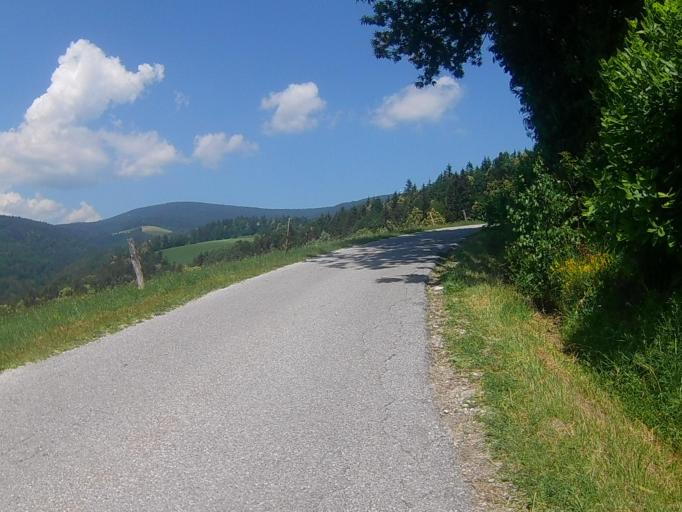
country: SI
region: Race-Fram
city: Morje
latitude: 46.4780
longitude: 15.5870
